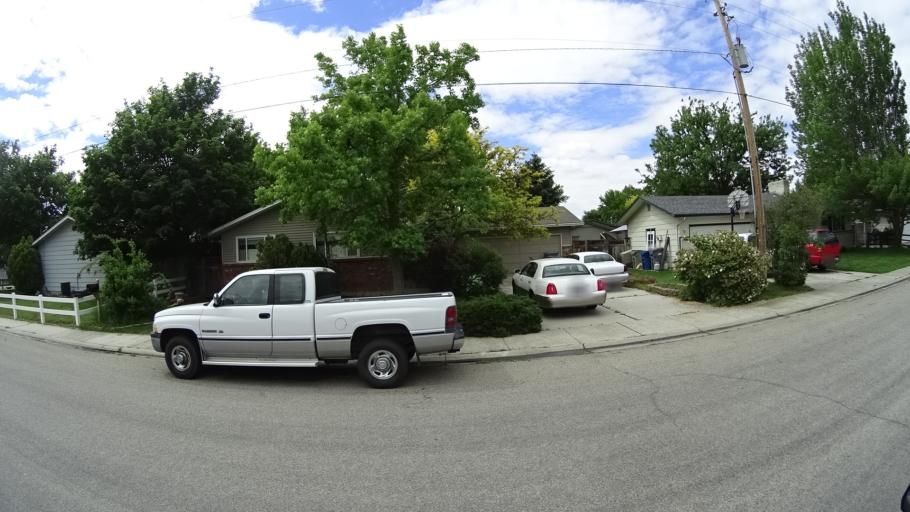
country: US
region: Idaho
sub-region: Ada County
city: Boise
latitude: 43.5715
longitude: -116.1674
